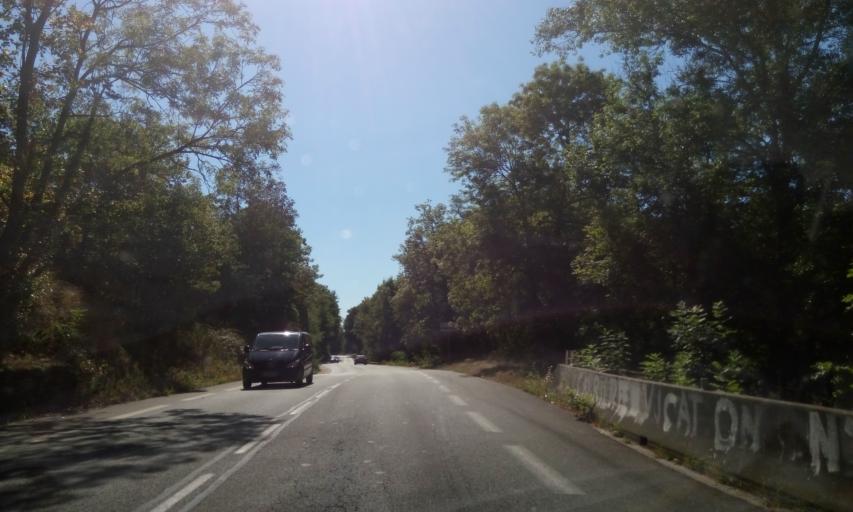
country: FR
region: Rhone-Alpes
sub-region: Departement du Rhone
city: Saint-Verand
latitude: 45.9381
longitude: 4.5453
